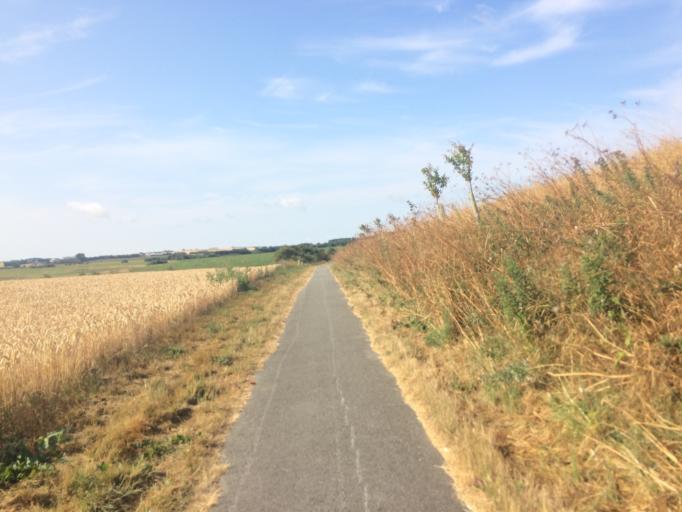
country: DK
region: Central Jutland
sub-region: Holstebro Kommune
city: Vinderup
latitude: 56.6245
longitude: 8.7809
